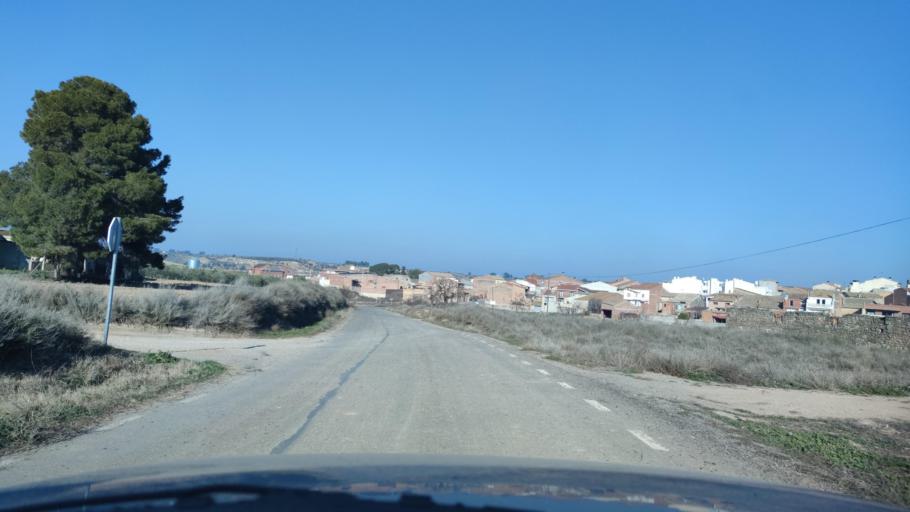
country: ES
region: Catalonia
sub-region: Provincia de Lleida
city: Torrebesses
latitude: 41.4569
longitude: 0.5586
